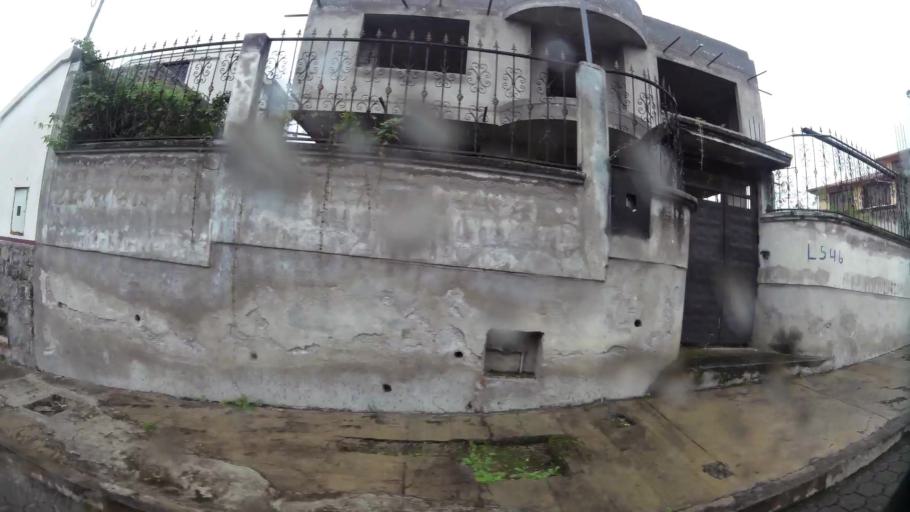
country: EC
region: Pichincha
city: Sangolqui
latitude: -0.3197
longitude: -78.4366
